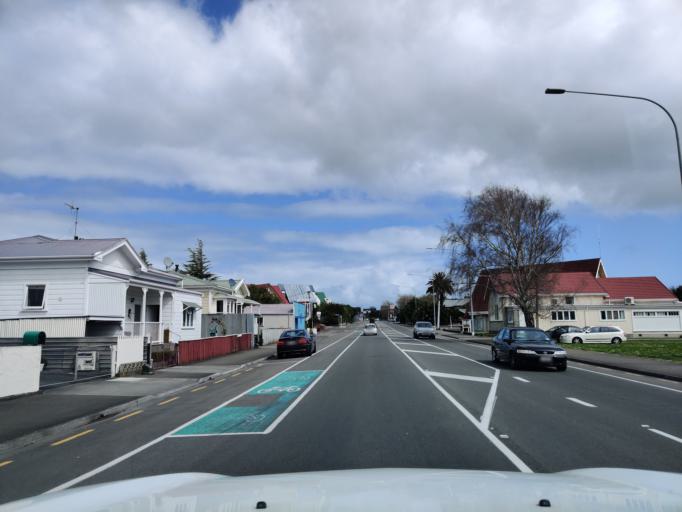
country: NZ
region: Manawatu-Wanganui
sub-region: Wanganui District
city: Wanganui
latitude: -39.9253
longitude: 175.0462
